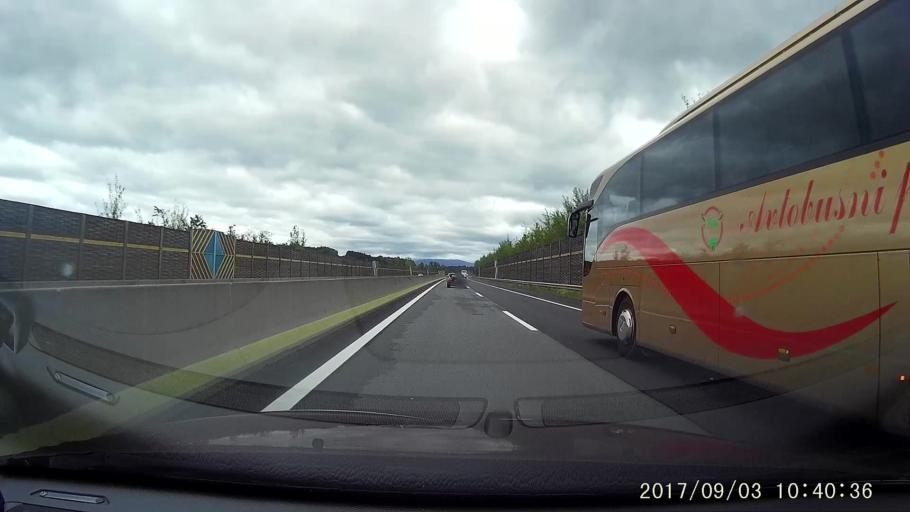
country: AT
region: Styria
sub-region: Politischer Bezirk Hartberg-Fuerstenfeld
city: Sebersdorf
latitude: 47.2303
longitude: 15.9950
